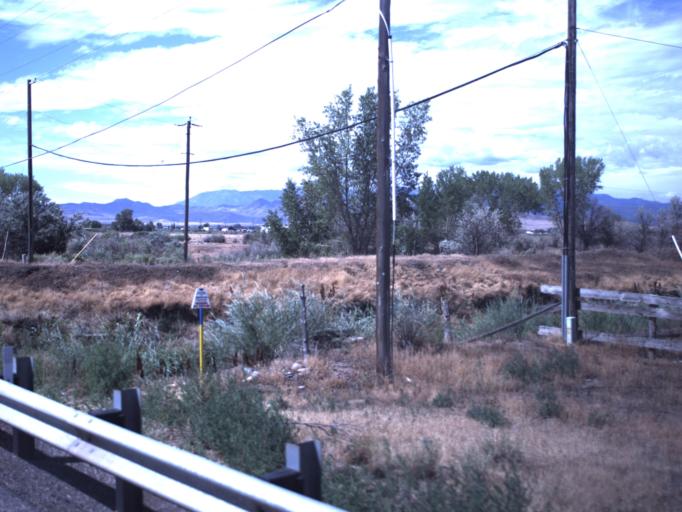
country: US
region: Utah
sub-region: Sevier County
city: Monroe
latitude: 38.6775
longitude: -112.1213
